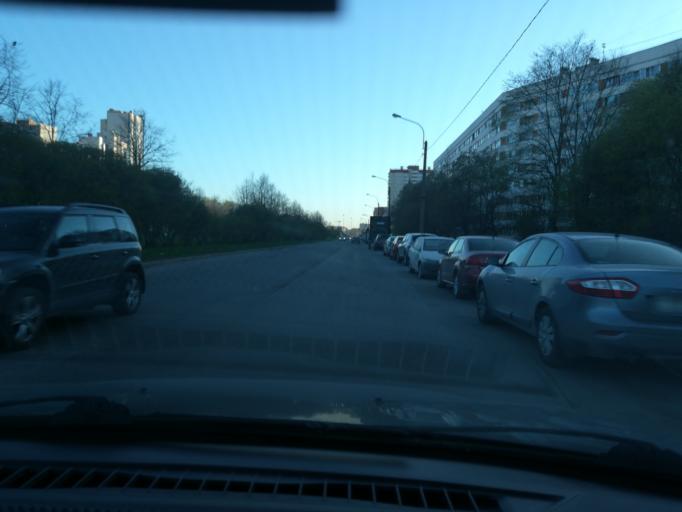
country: RU
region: St.-Petersburg
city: Dachnoye
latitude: 59.8567
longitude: 30.2452
